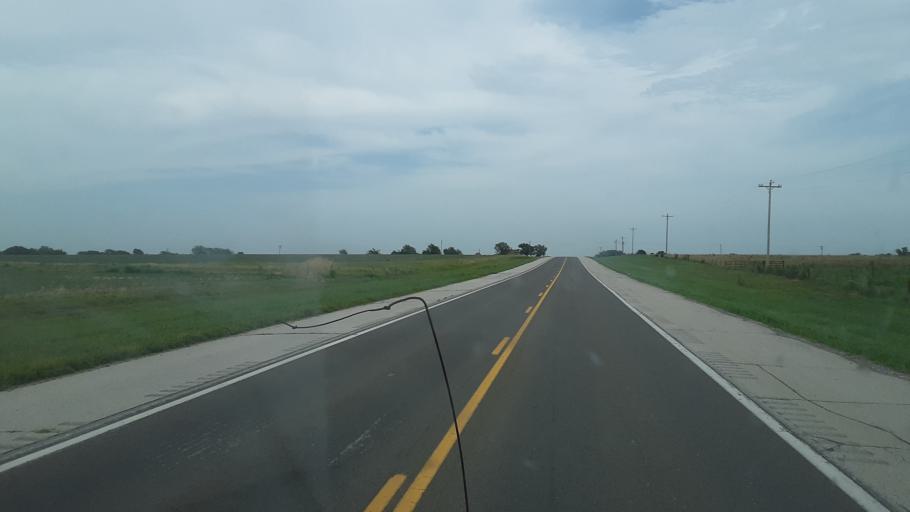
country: US
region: Kansas
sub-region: Allen County
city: Iola
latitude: 37.9220
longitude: -95.4691
